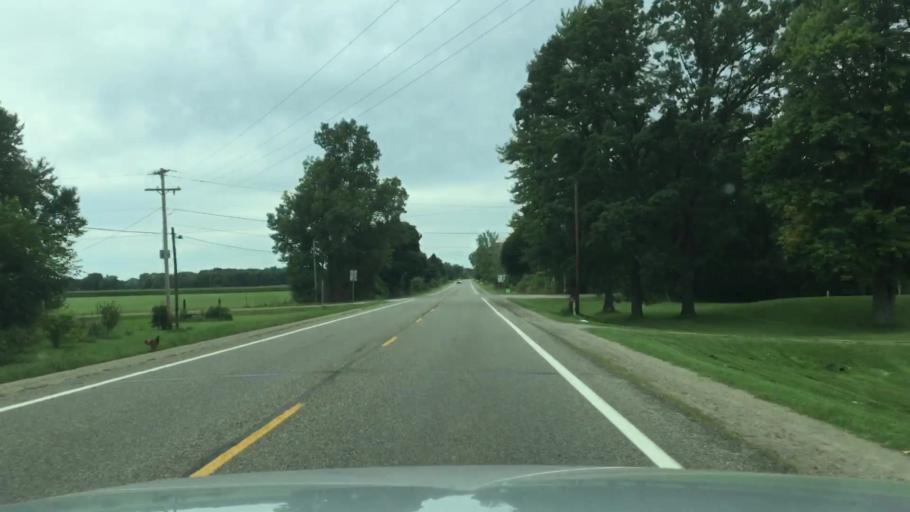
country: US
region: Michigan
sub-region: Shiawassee County
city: Durand
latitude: 42.9316
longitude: -84.0070
